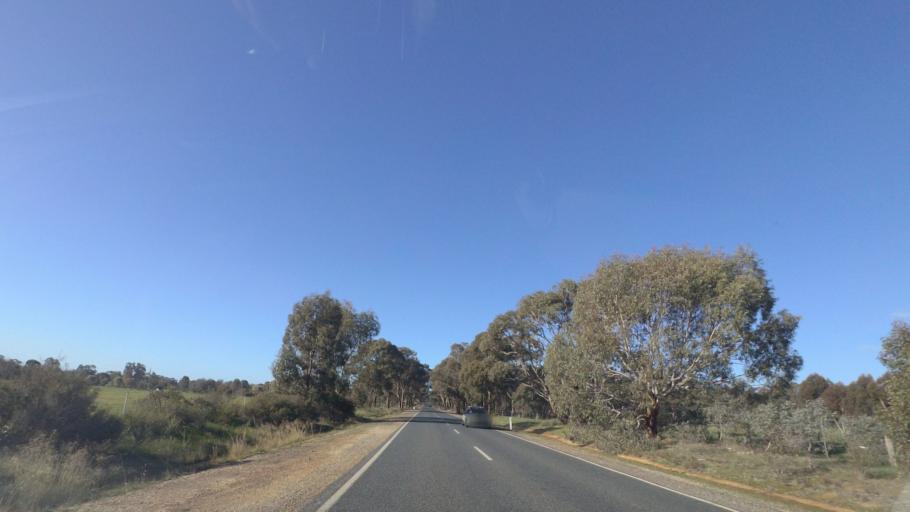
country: AU
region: Victoria
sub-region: Greater Bendigo
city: Epsom
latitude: -36.6747
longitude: 144.3984
